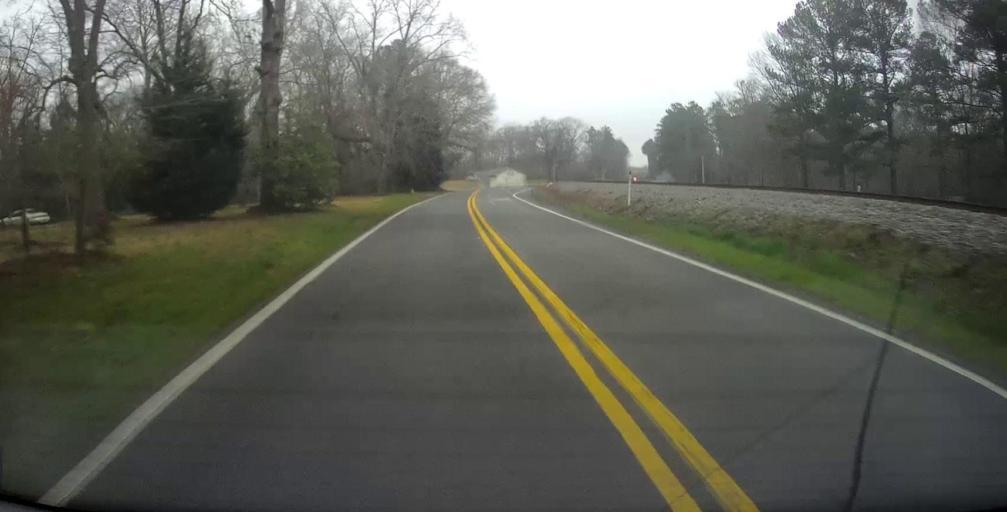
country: US
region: Georgia
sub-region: Spalding County
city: East Griffin
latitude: 33.1951
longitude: -84.2161
